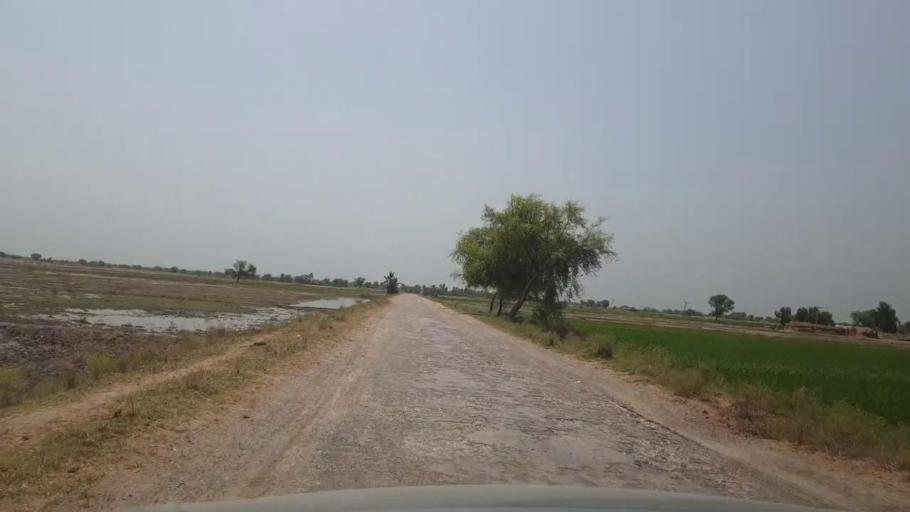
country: PK
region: Sindh
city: Garhi Yasin
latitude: 27.9151
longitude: 68.4039
